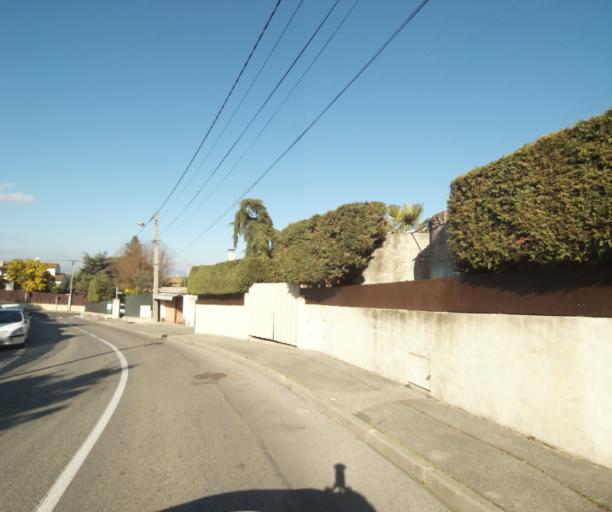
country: FR
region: Provence-Alpes-Cote d'Azur
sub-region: Departement des Alpes-Maritimes
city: Biot
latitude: 43.6018
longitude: 7.1090
